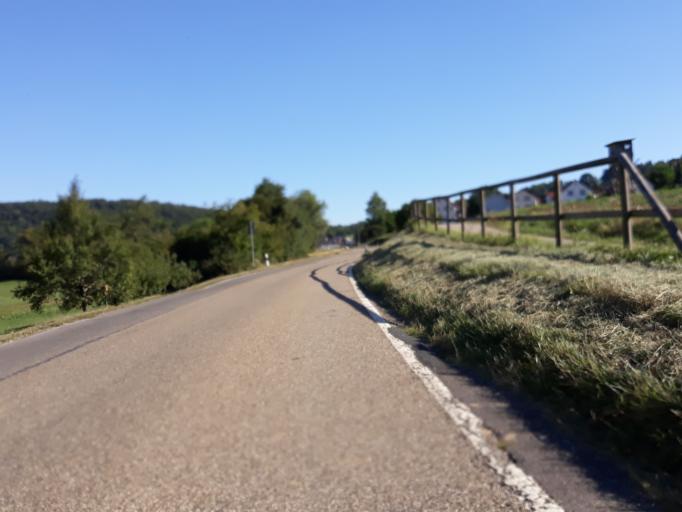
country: DE
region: Baden-Wuerttemberg
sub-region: Regierungsbezirk Stuttgart
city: Aidlingen
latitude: 48.6841
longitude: 8.9020
